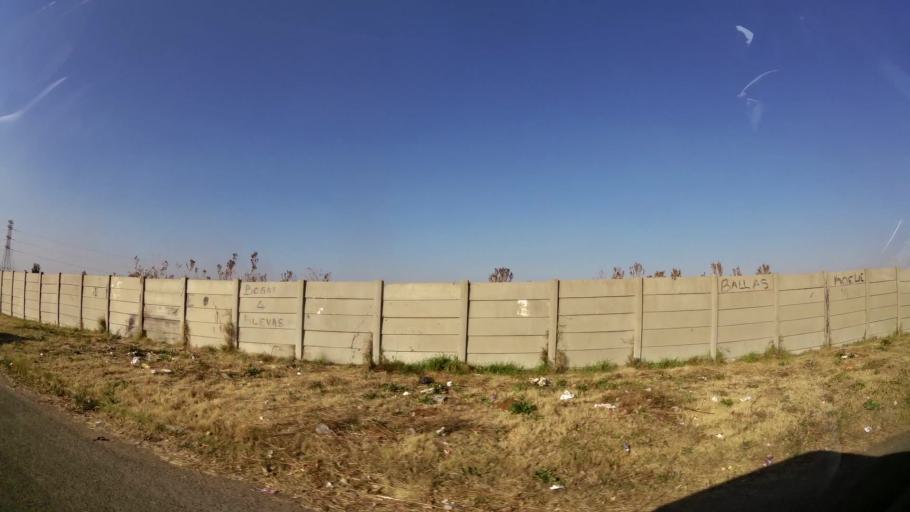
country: ZA
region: Gauteng
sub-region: West Rand District Municipality
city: Randfontein
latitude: -26.1929
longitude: 27.7019
